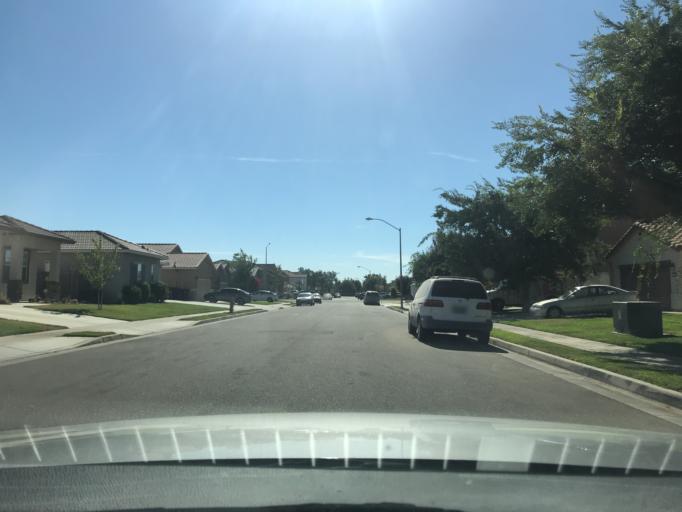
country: US
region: California
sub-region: Merced County
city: Atwater
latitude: 37.3418
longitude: -120.5733
